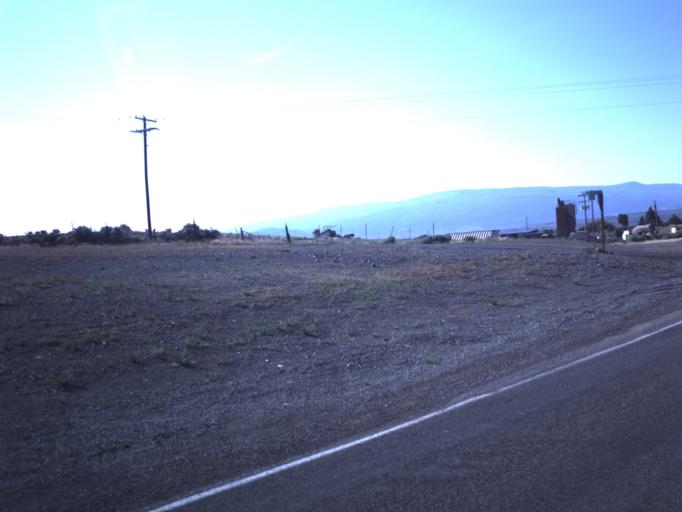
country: US
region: Utah
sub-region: Wayne County
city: Loa
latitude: 38.4121
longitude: -111.6206
